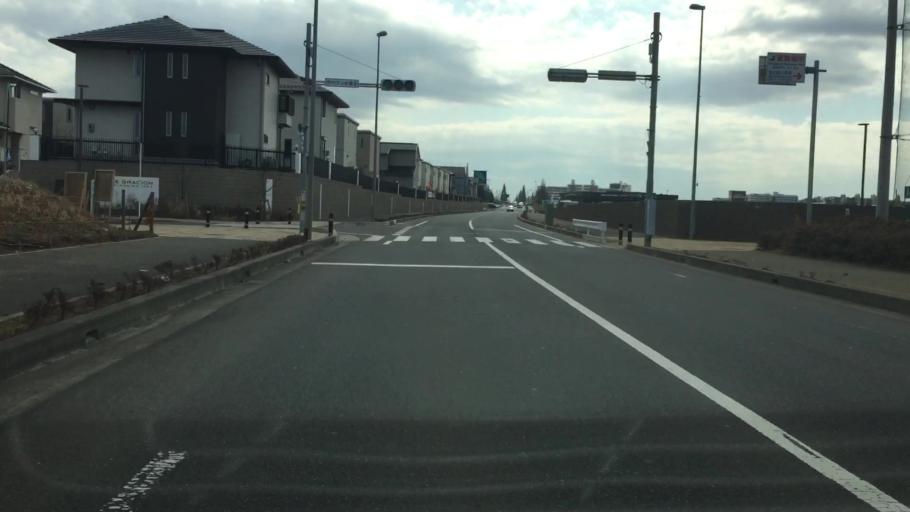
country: JP
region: Ibaraki
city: Ryugasaki
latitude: 35.8115
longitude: 140.1618
